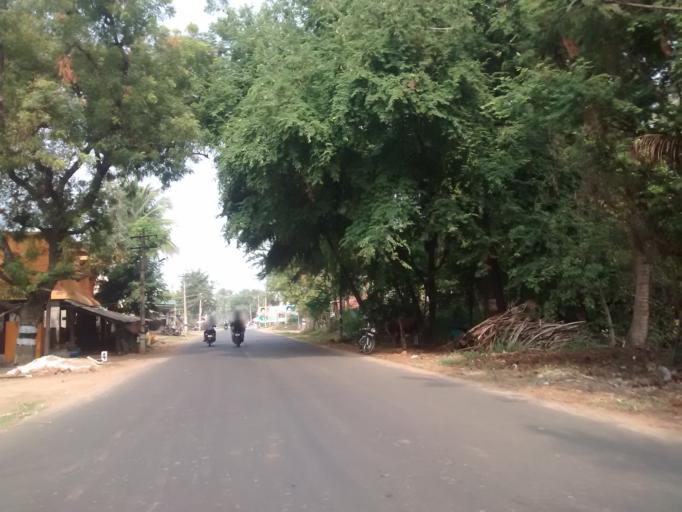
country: IN
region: Tamil Nadu
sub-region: Krishnagiri
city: Kaverippattanam
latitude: 12.4683
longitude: 78.2027
